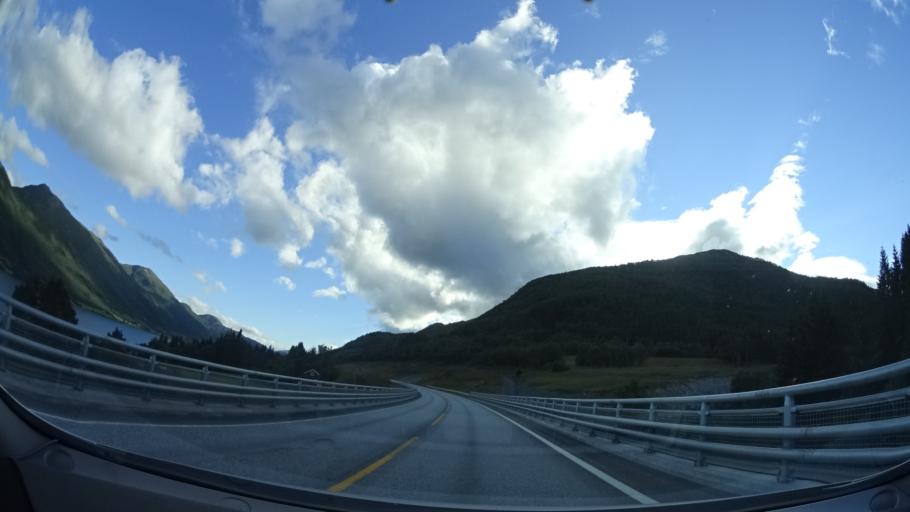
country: NO
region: More og Romsdal
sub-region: Gjemnes
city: Batnfjordsora
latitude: 62.9280
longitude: 7.7106
